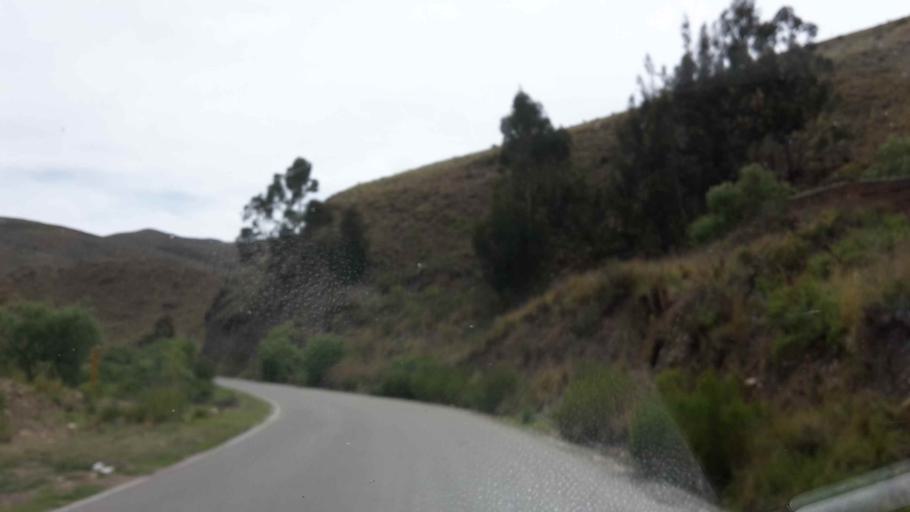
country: BO
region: Cochabamba
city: Colomi
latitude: -17.3996
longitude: -65.8051
